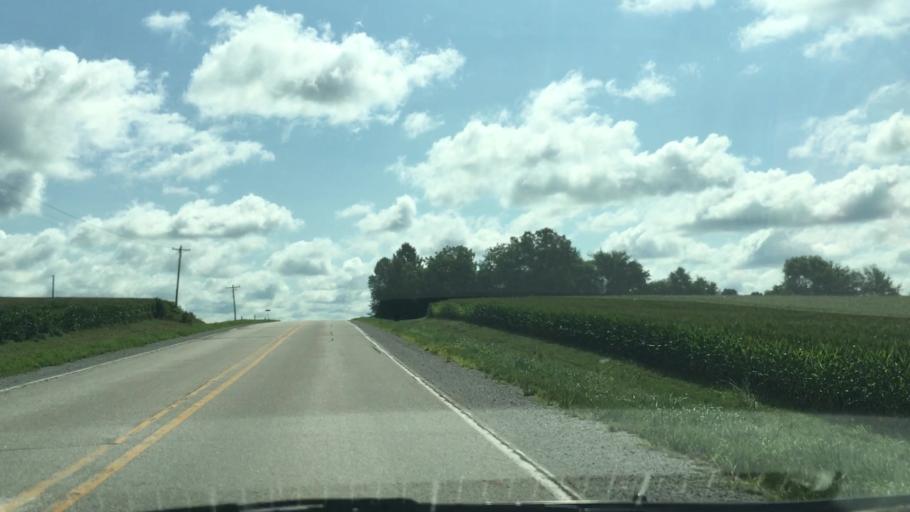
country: US
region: Iowa
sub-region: Johnson County
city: Solon
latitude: 41.8310
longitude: -91.4562
